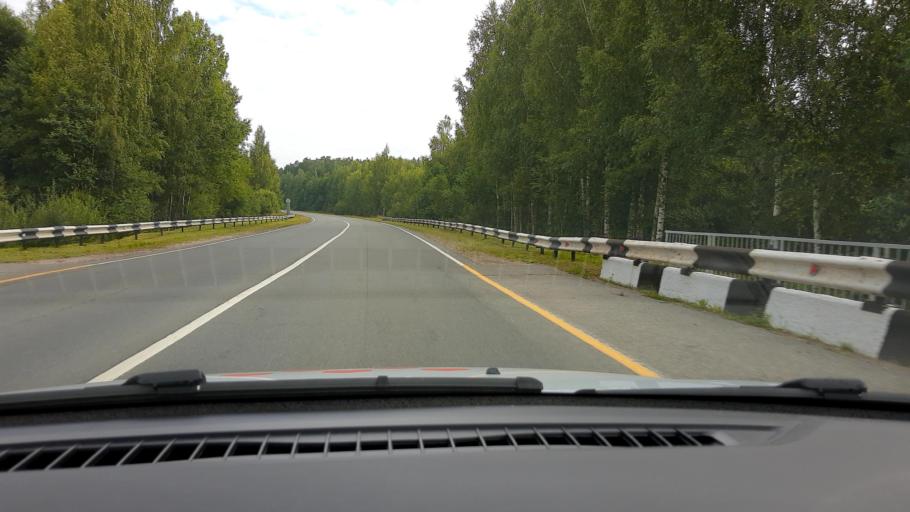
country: RU
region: Nizjnij Novgorod
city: Semenov
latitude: 56.7952
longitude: 44.4587
